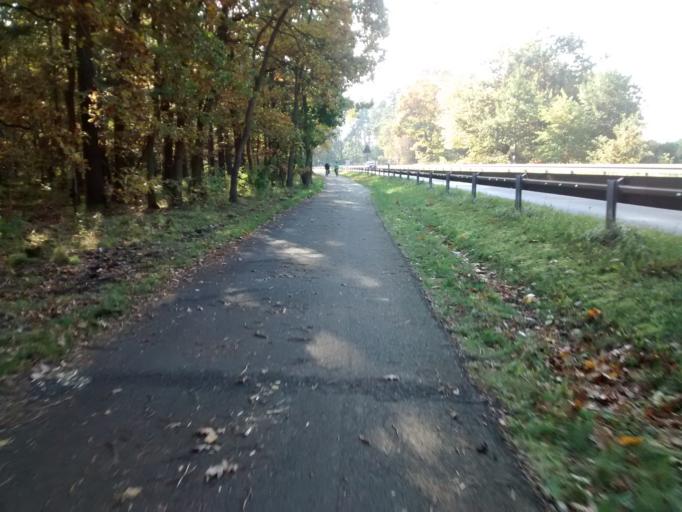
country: DE
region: Brandenburg
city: Hennigsdorf
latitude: 52.6429
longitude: 13.2260
